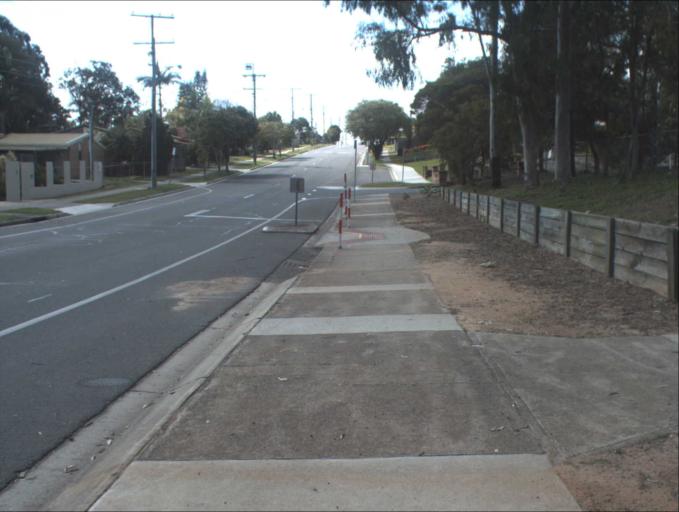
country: AU
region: Queensland
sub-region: Logan
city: Park Ridge South
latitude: -27.6696
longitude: 153.0343
